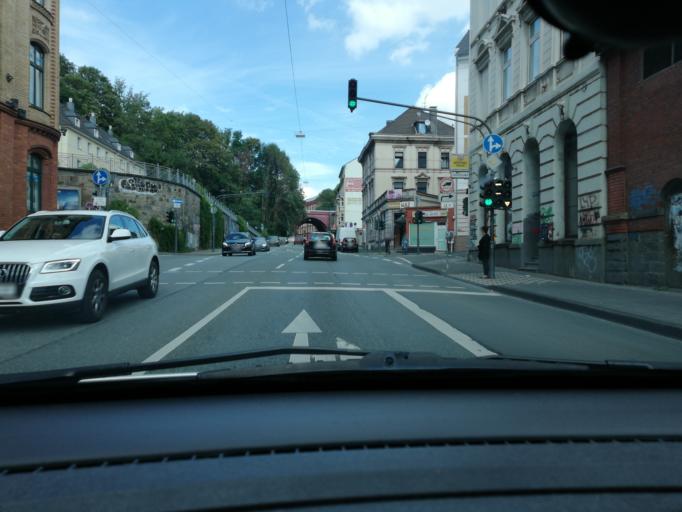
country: DE
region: North Rhine-Westphalia
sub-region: Regierungsbezirk Dusseldorf
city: Wuppertal
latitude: 51.2664
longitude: 7.1477
